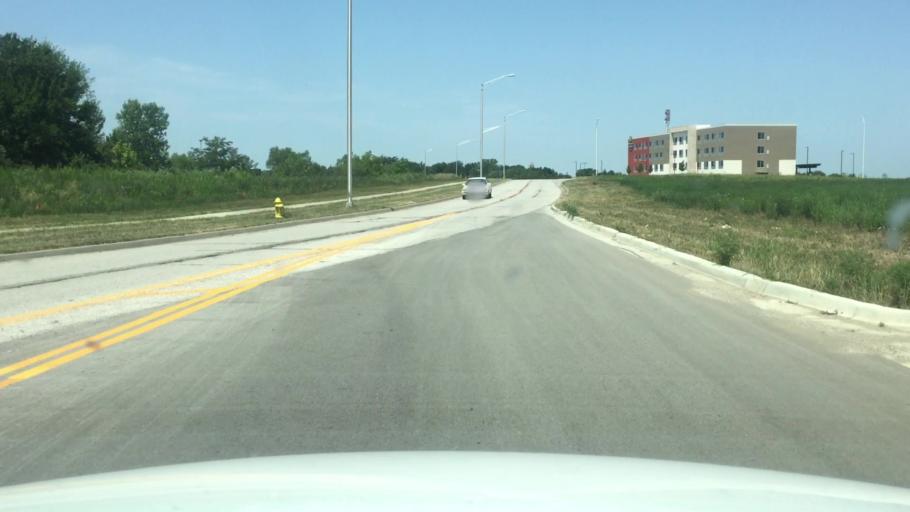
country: US
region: Missouri
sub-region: Jackson County
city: Lees Summit
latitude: 38.9316
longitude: -94.3931
